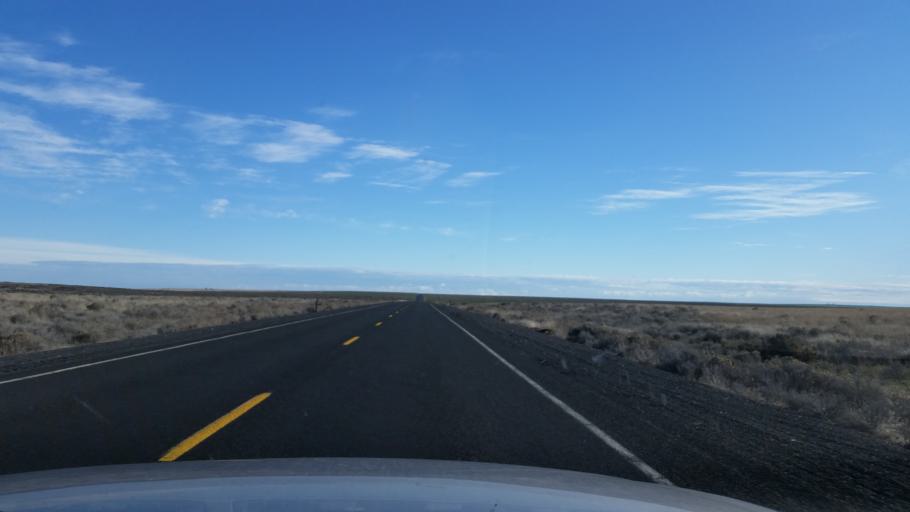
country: US
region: Washington
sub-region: Grant County
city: Moses Lake
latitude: 47.3605
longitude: -118.9640
